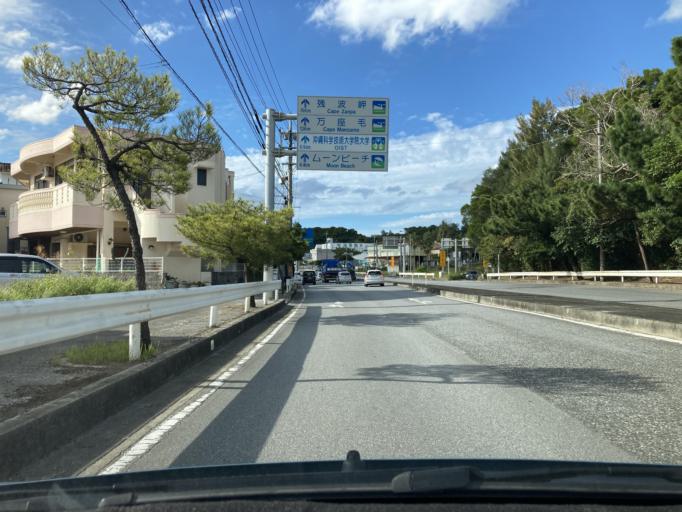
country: JP
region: Okinawa
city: Ishikawa
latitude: 26.4341
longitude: 127.8302
